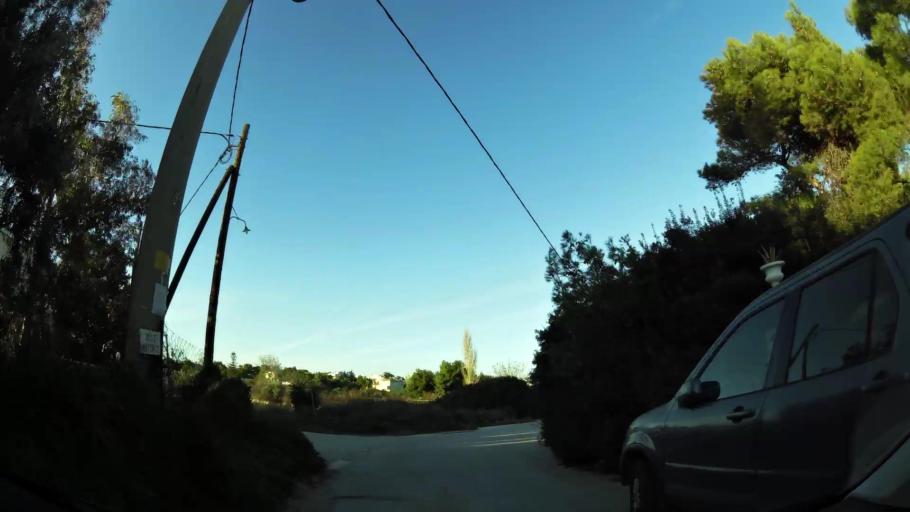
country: GR
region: Attica
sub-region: Nomarchia Anatolikis Attikis
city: Rafina
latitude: 38.0060
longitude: 24.0163
